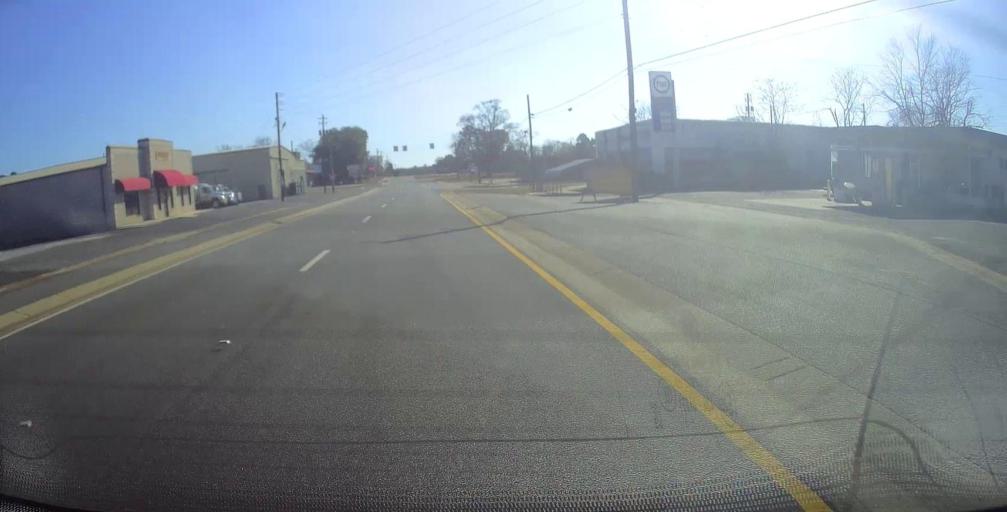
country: US
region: Georgia
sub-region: Taylor County
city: Butler
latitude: 32.5565
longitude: -84.2384
